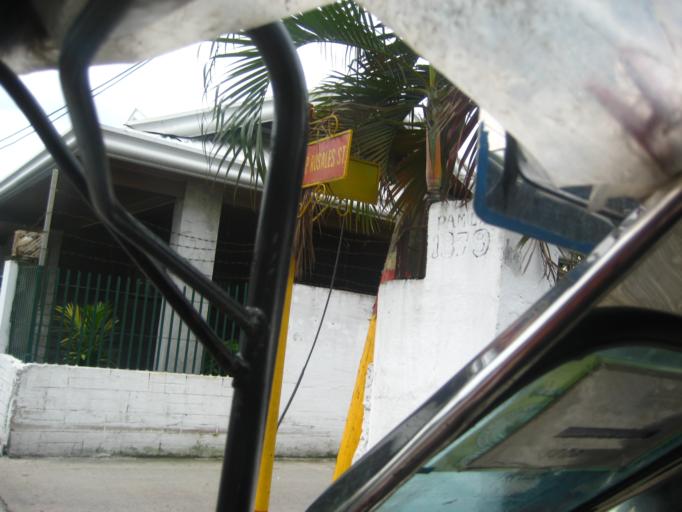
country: PH
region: Calabarzon
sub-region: Province of Rizal
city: Pateros
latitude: 14.5423
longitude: 121.0678
